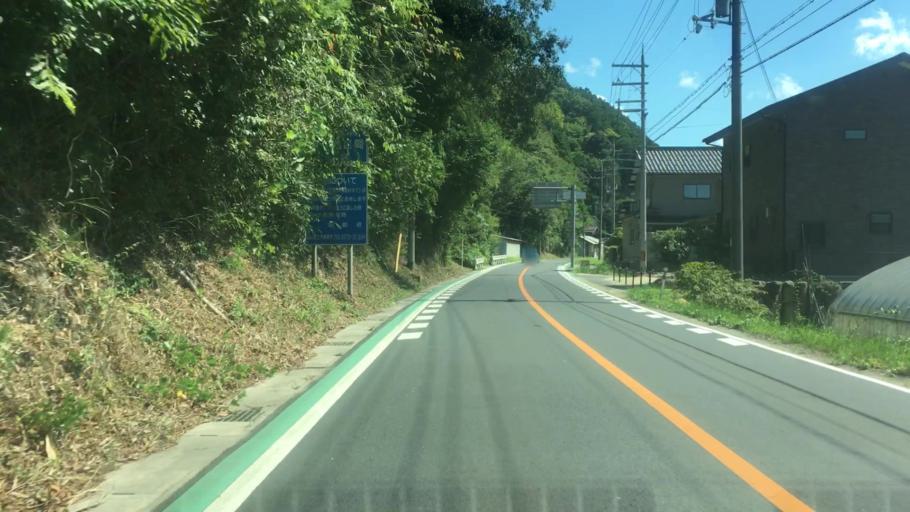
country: JP
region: Hyogo
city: Toyooka
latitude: 35.5983
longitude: 134.9045
